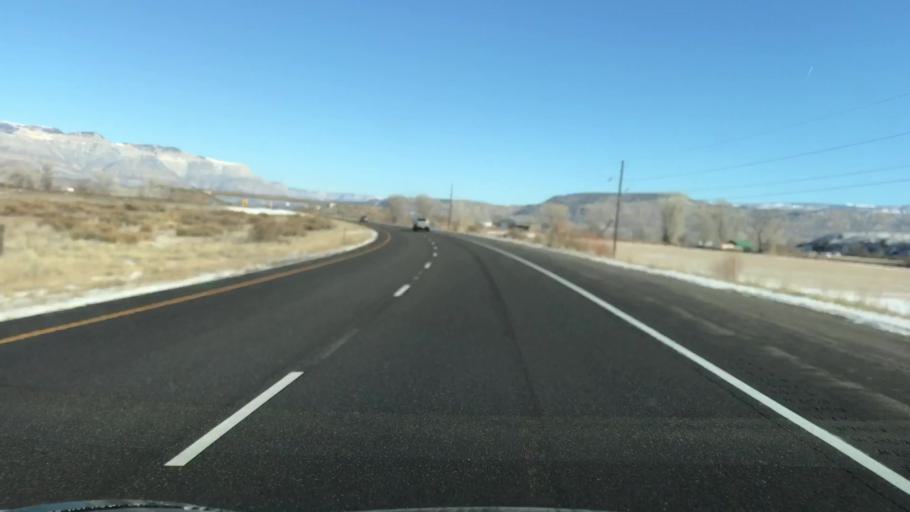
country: US
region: Colorado
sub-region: Mesa County
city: Palisade
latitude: 39.2817
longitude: -108.2315
